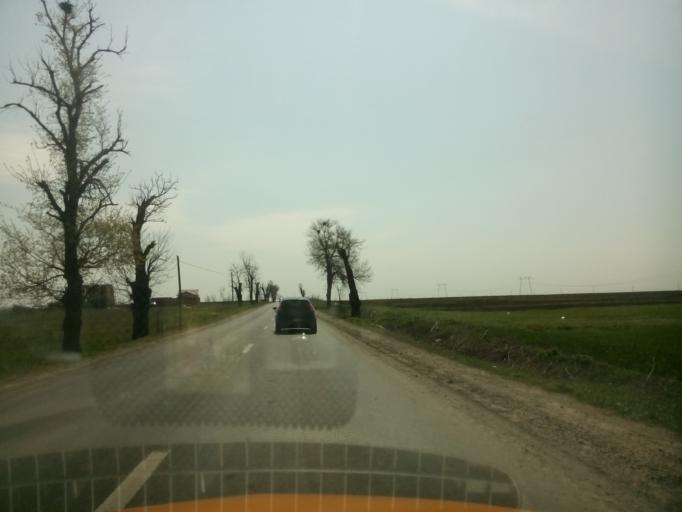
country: RO
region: Calarasi
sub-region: Comuna Frumusani
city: Frumusani
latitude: 44.2734
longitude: 26.3410
